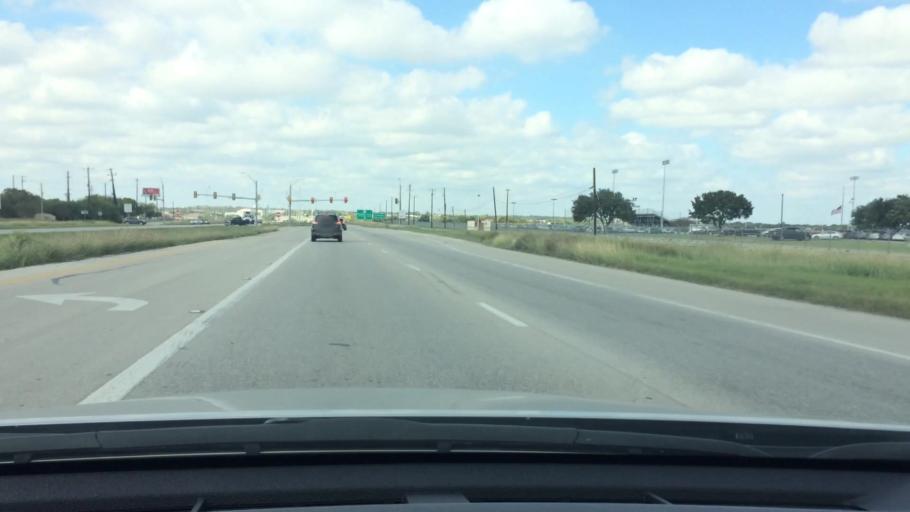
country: US
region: Texas
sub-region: Bexar County
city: Converse
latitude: 29.5263
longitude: -98.2963
